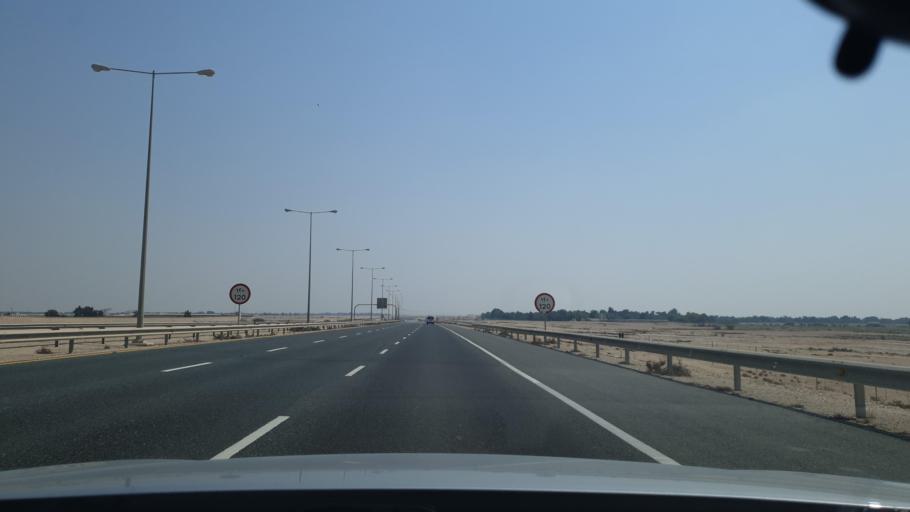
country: QA
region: Al Khawr
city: Al Khawr
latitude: 25.7850
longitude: 51.3976
